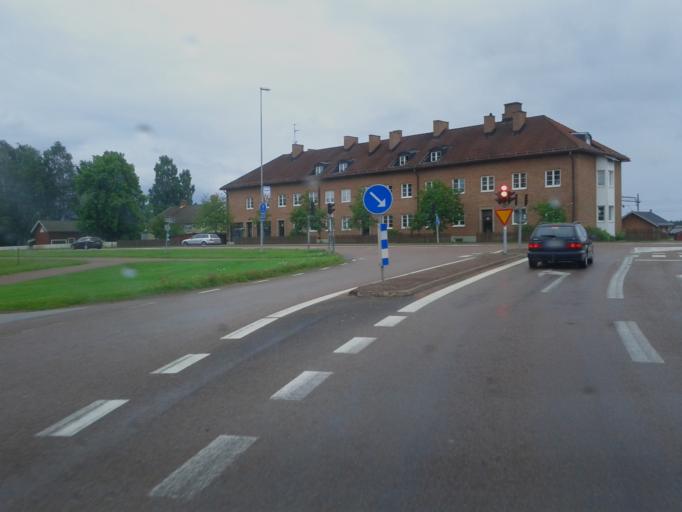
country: SE
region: Dalarna
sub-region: Mora Kommun
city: Mora
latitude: 61.0099
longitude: 14.5510
